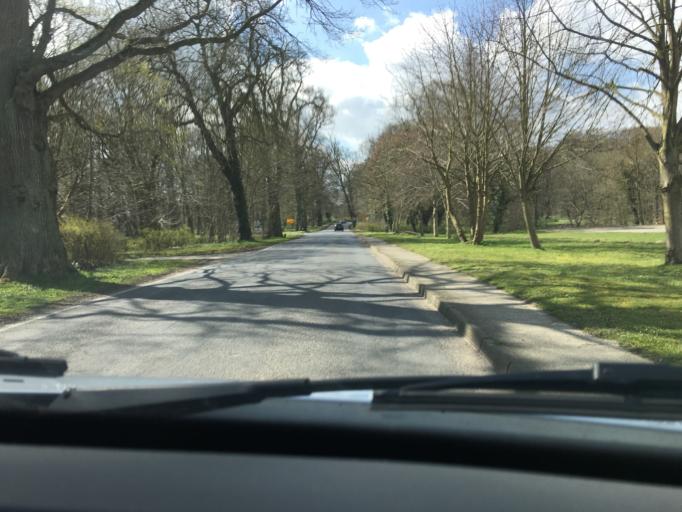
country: DE
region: Mecklenburg-Vorpommern
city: Bad Sulze
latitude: 54.1788
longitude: 12.6580
